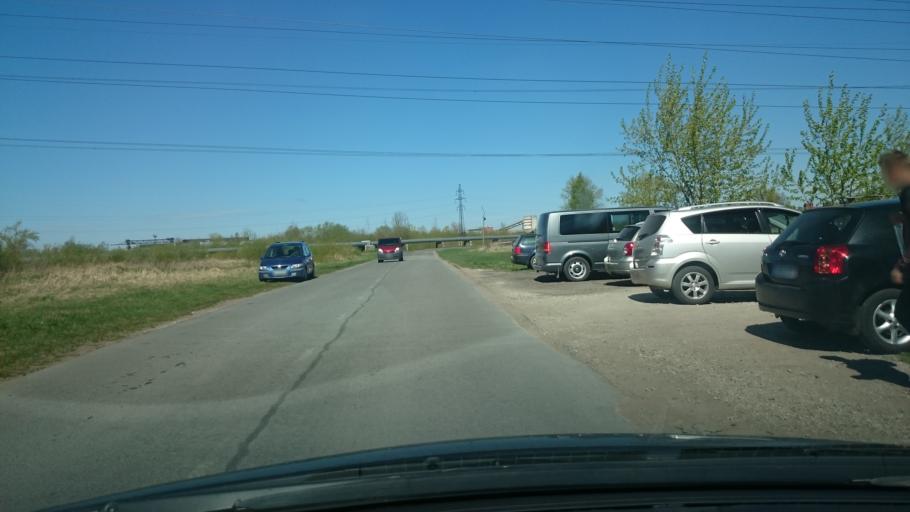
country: EE
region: Ida-Virumaa
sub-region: Narva linn
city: Narva
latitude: 59.3502
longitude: 28.1728
